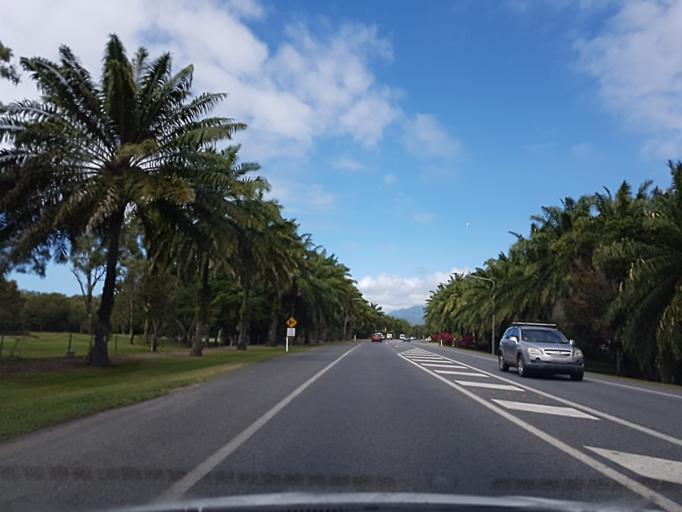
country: AU
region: Queensland
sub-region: Cairns
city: Port Douglas
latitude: -16.5085
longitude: 145.4631
